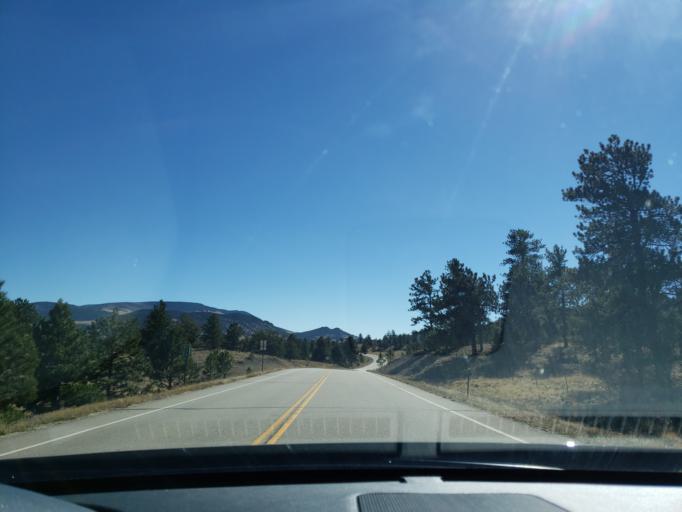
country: US
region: Colorado
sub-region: Chaffee County
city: Buena Vista
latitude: 38.8810
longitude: -105.6785
